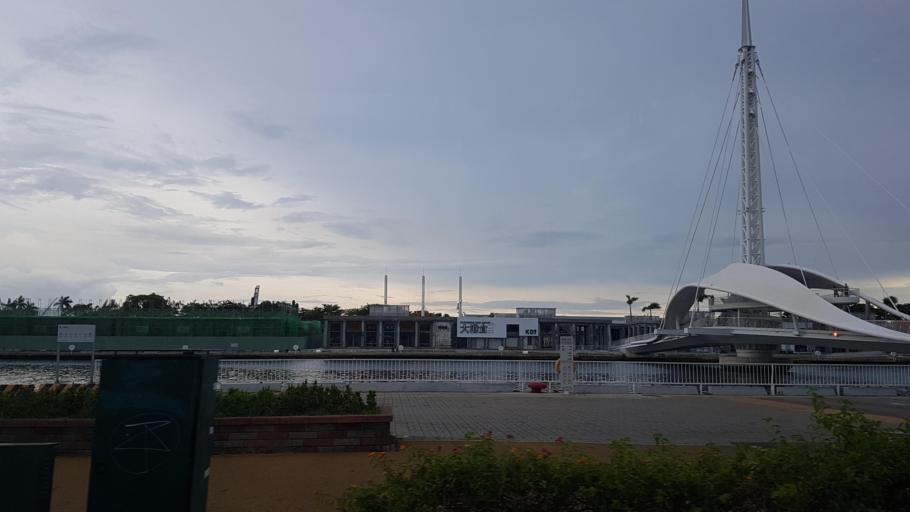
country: TW
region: Kaohsiung
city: Kaohsiung
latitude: 22.6182
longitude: 120.2847
